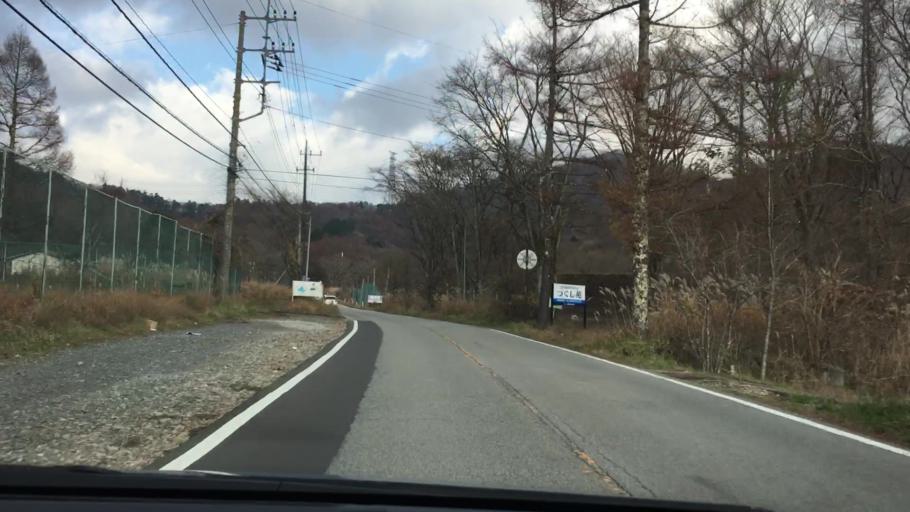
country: JP
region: Shizuoka
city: Gotemba
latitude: 35.4430
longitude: 138.9246
